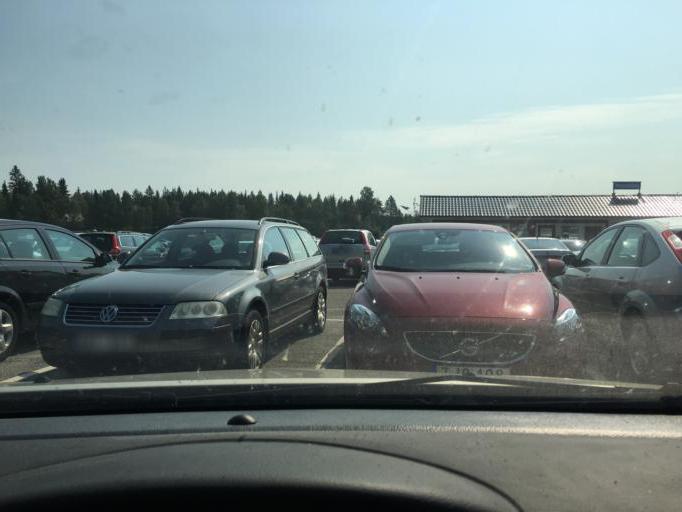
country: SE
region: Norrbotten
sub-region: Kalix Kommun
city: Kalix
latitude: 65.7635
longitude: 23.1932
